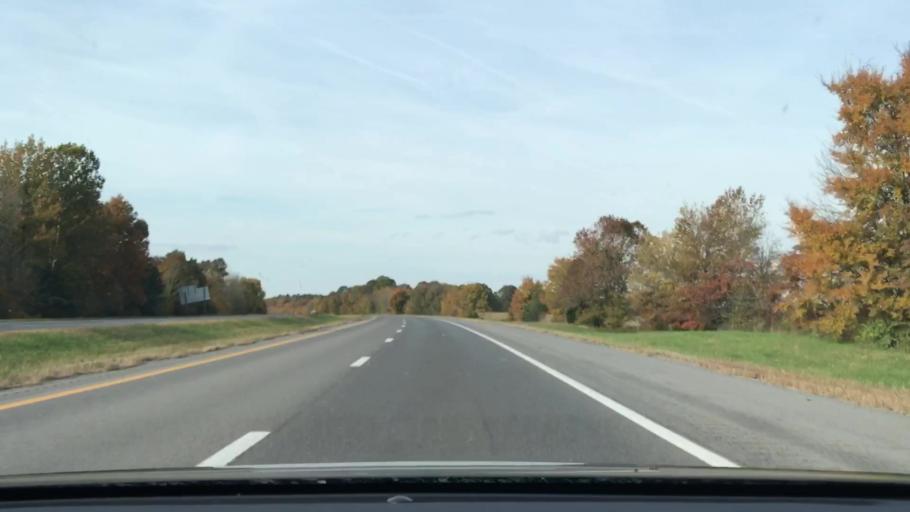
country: US
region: Kentucky
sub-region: Marshall County
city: Benton
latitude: 36.8465
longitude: -88.4050
